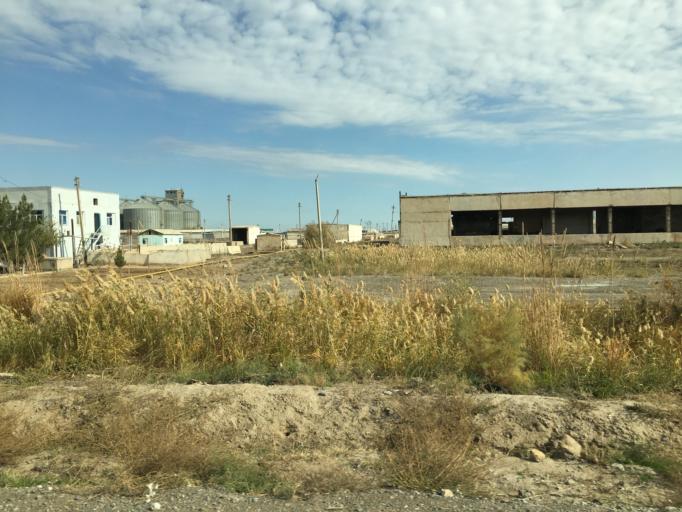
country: TM
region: Ahal
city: Tejen
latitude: 37.3205
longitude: 61.0902
